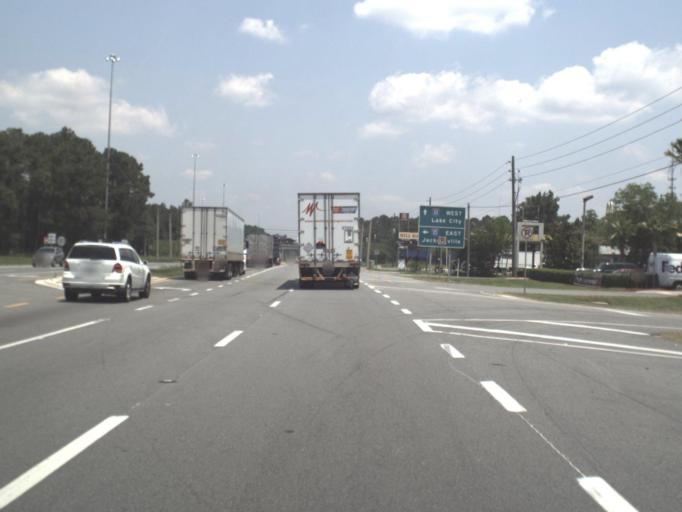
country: US
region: Florida
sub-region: Duval County
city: Baldwin
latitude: 30.2853
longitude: -81.9827
